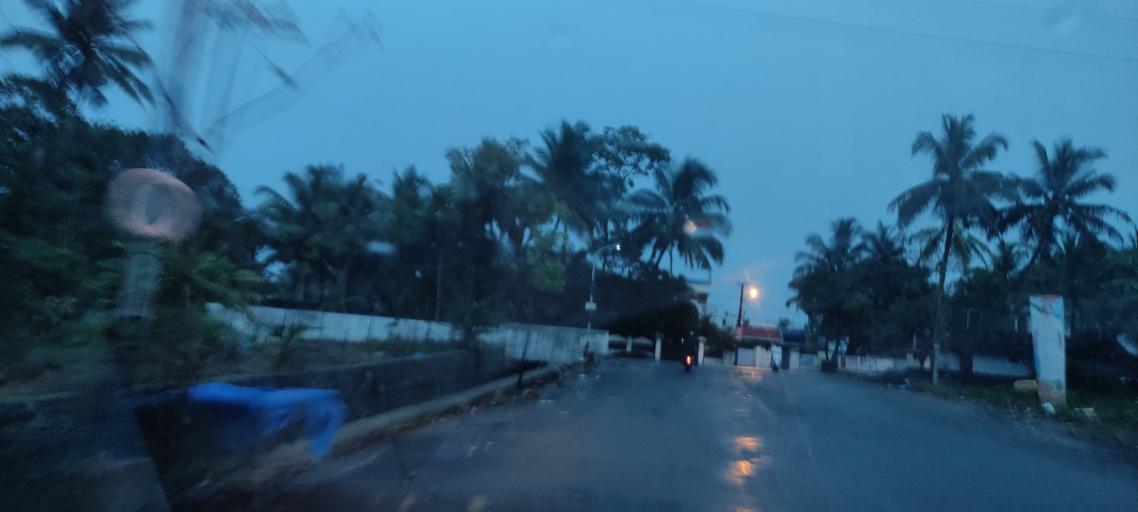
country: IN
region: Kerala
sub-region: Ernakulam
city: Cochin
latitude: 9.9205
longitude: 76.2881
